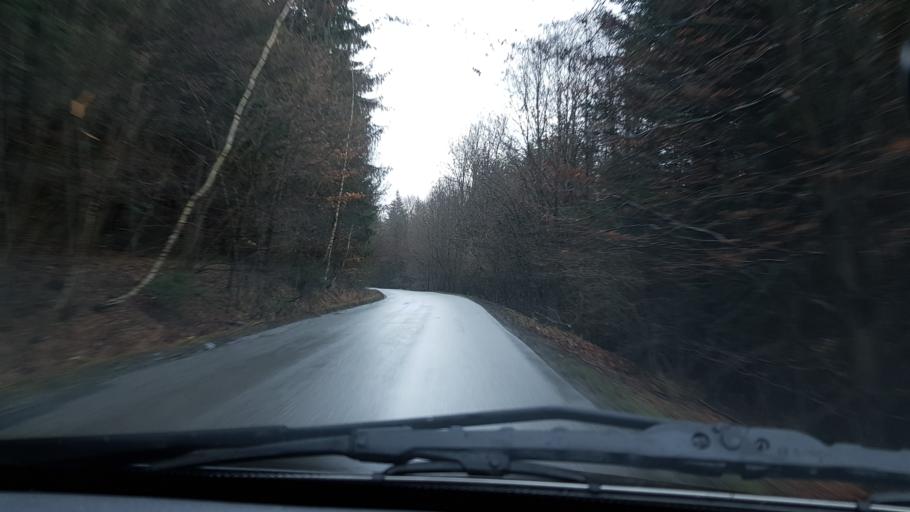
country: PL
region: Lesser Poland Voivodeship
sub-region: Powiat suski
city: Jordanow
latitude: 49.6334
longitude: 19.8396
